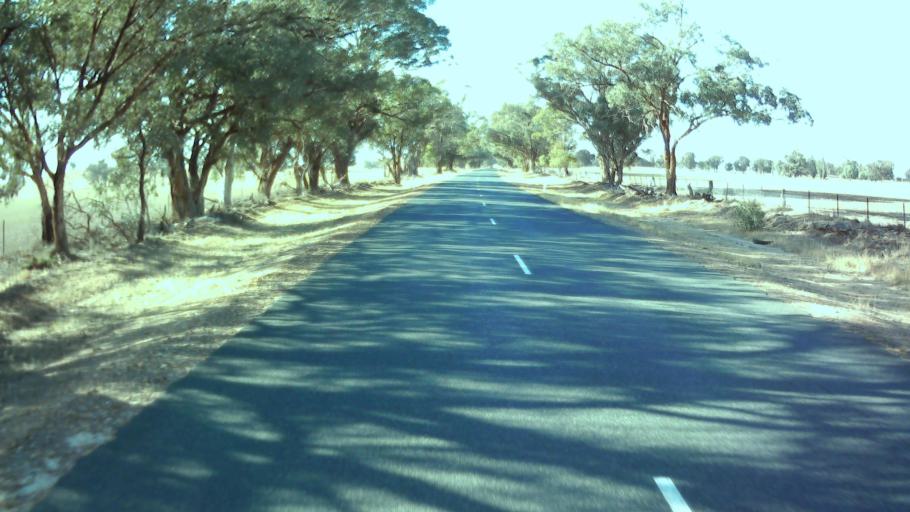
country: AU
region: New South Wales
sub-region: Weddin
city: Grenfell
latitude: -33.9572
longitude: 148.1395
